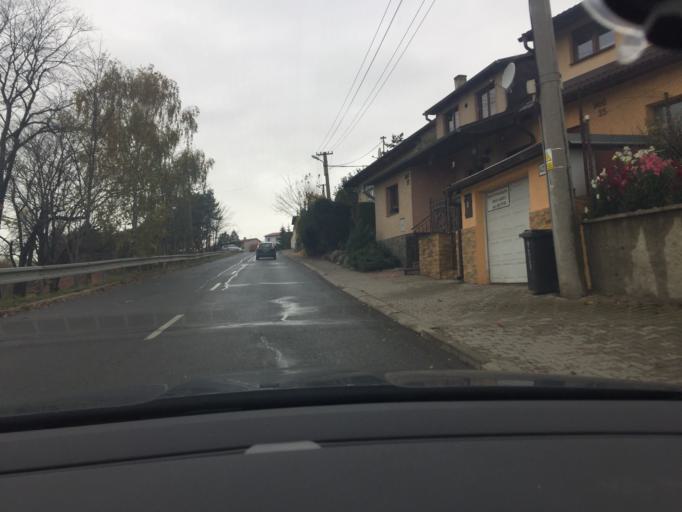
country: SK
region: Presovsky
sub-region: Okres Poprad
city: Poprad
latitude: 49.0639
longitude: 20.3120
